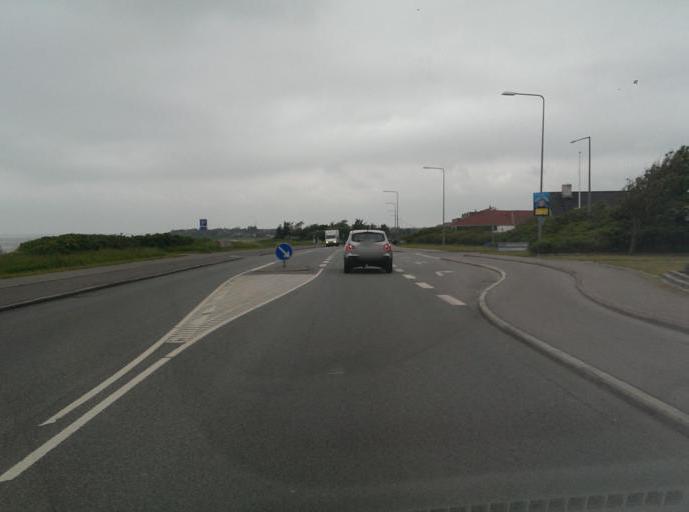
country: DK
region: South Denmark
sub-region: Fano Kommune
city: Nordby
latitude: 55.5055
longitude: 8.3842
